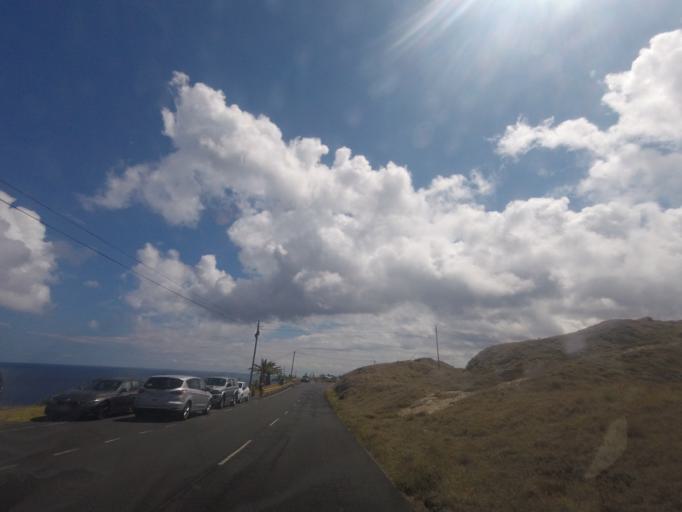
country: PT
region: Madeira
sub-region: Machico
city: Canical
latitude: 32.7447
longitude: -16.7158
